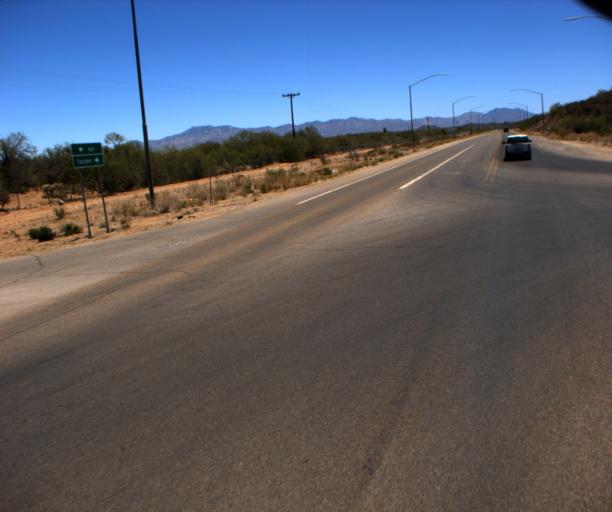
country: US
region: Arizona
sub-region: Pima County
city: Sells
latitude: 31.9213
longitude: -111.8901
